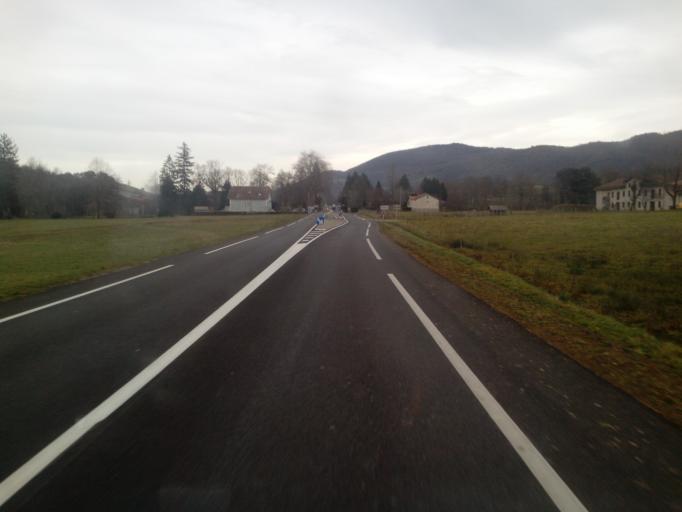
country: FR
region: Midi-Pyrenees
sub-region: Departement de l'Ariege
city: Foix
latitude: 43.0088
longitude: 1.4591
